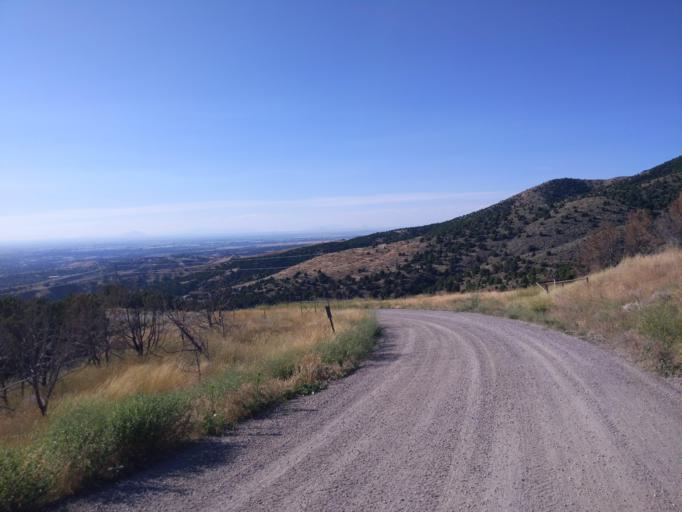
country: US
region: Idaho
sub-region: Bannock County
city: Pocatello
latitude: 42.8524
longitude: -112.3806
